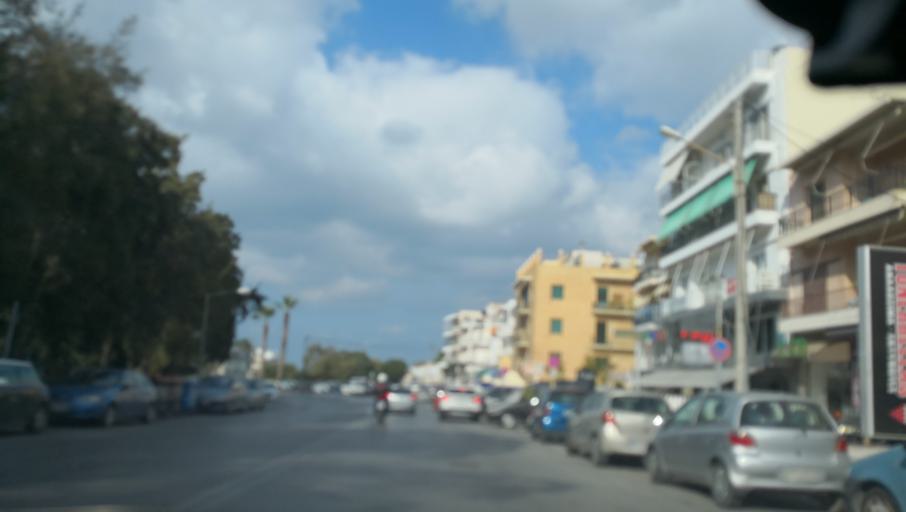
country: GR
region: Crete
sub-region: Nomos Irakleiou
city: Irakleion
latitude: 35.3355
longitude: 25.1389
